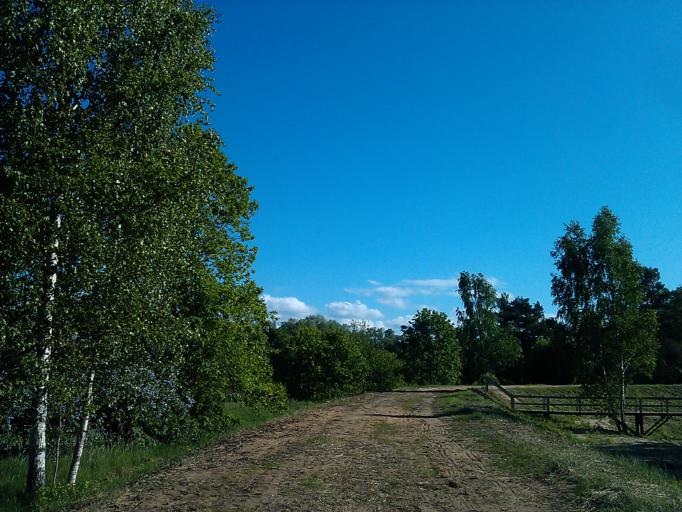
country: LV
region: Adazi
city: Adazi
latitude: 57.0965
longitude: 24.3300
